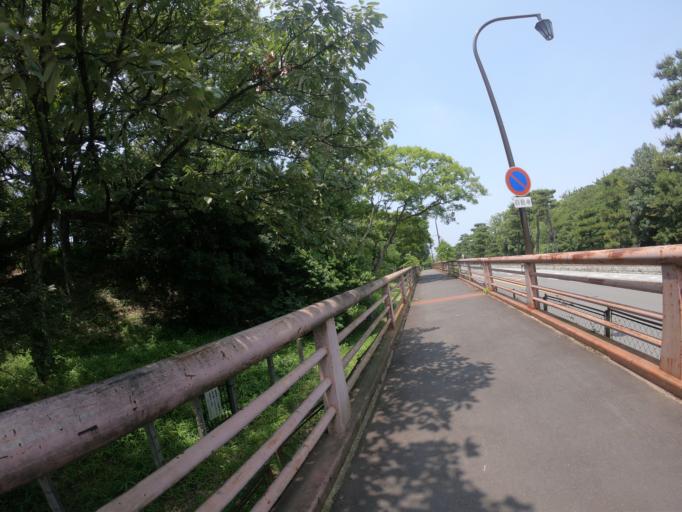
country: JP
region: Osaka
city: Sakai
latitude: 34.5613
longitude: 135.4837
